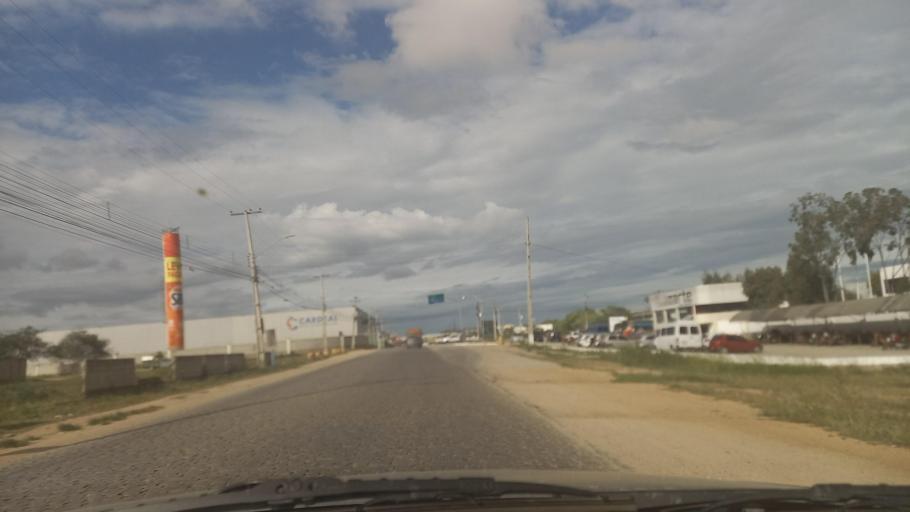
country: BR
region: Pernambuco
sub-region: Caruaru
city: Caruaru
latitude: -8.2891
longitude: -36.0136
